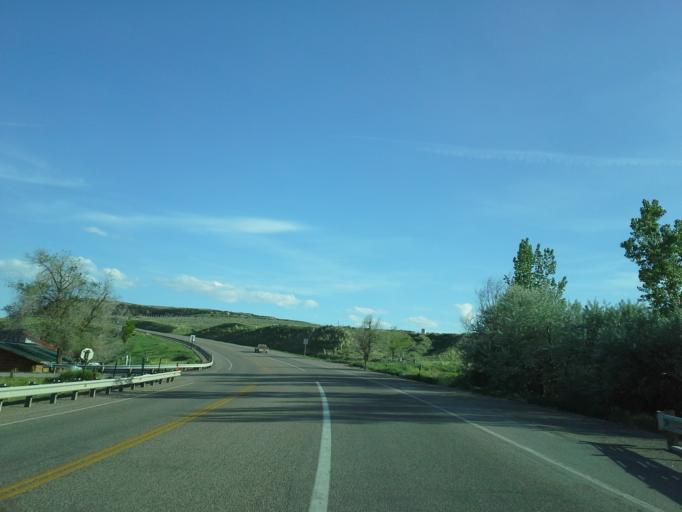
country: US
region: Wyoming
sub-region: Hot Springs County
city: Thermopolis
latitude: 43.6744
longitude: -108.2058
